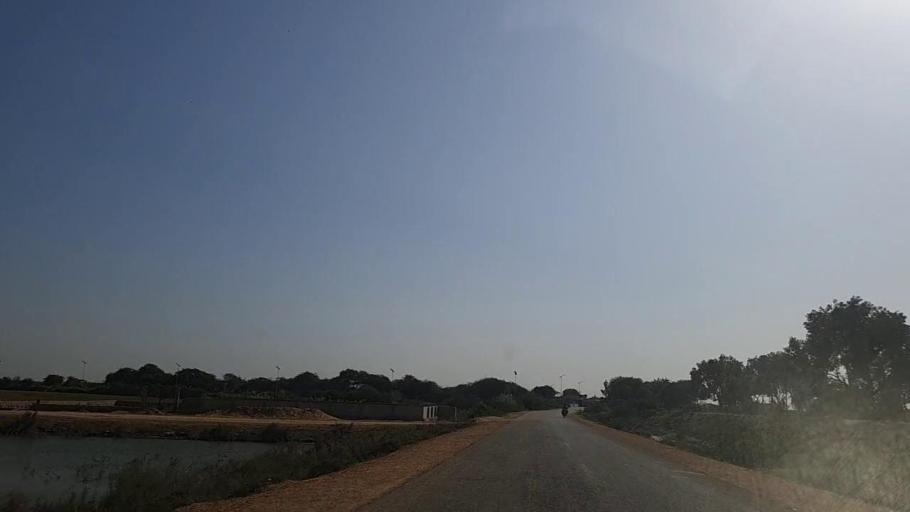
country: PK
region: Sindh
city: Jati
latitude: 24.4258
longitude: 68.2579
